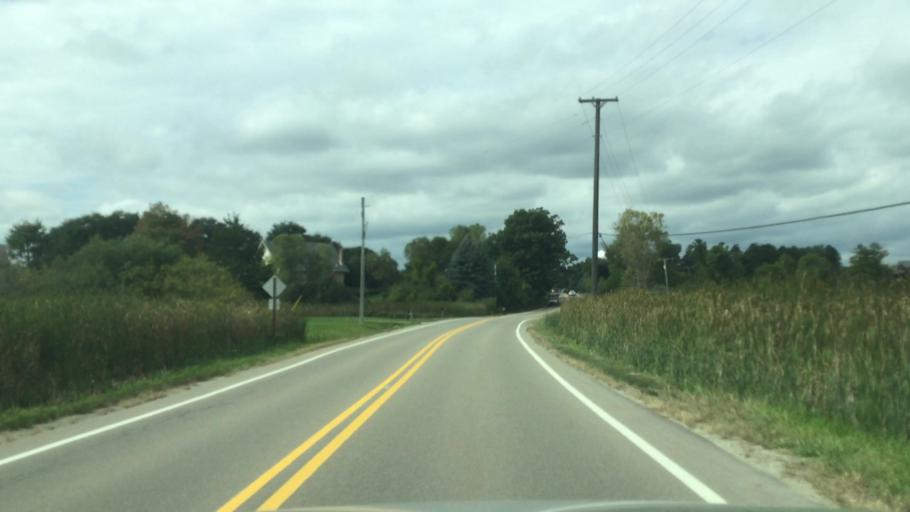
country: US
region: Michigan
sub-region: Livingston County
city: Brighton
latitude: 42.5494
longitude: -83.7791
